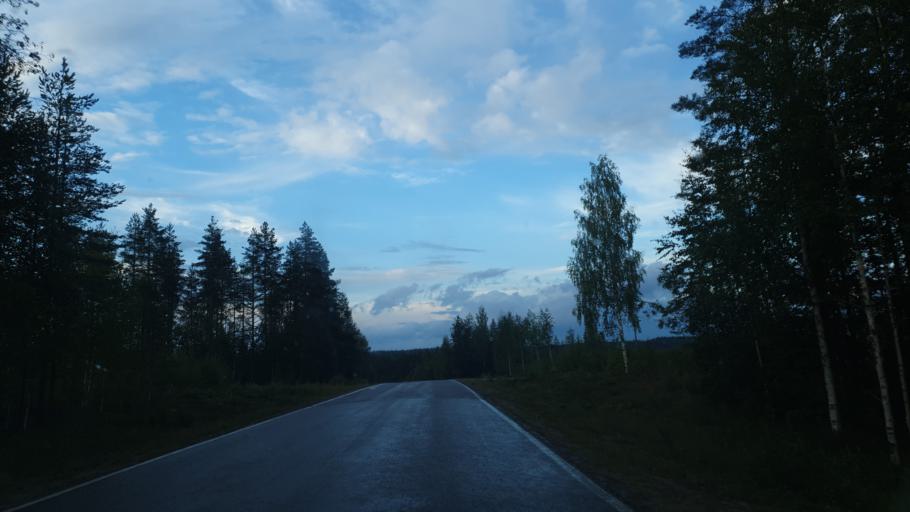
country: FI
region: North Karelia
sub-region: Pielisen Karjala
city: Lieksa
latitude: 63.7546
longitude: 29.8598
